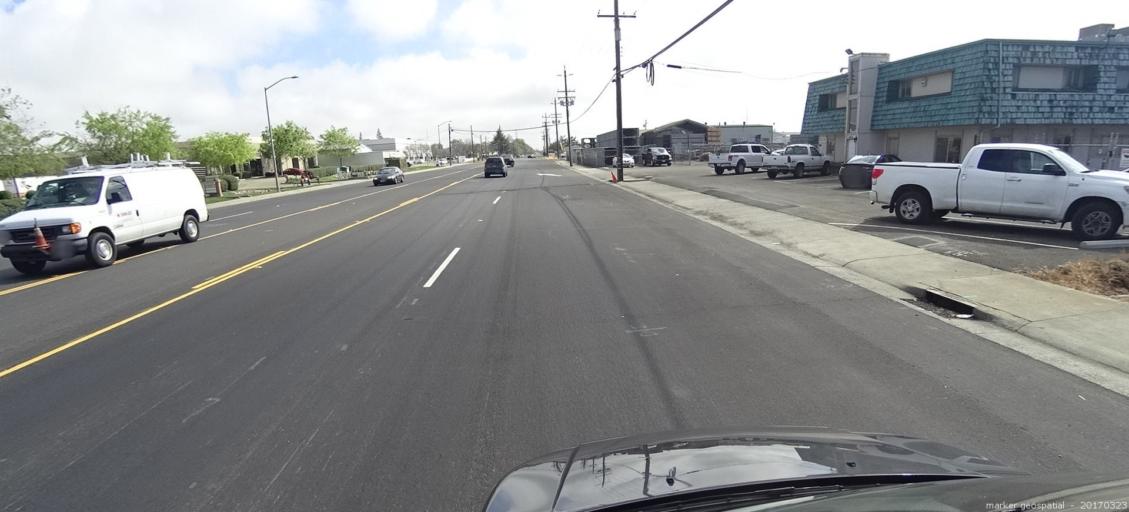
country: US
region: California
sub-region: Sacramento County
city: Florin
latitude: 38.5105
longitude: -121.3893
